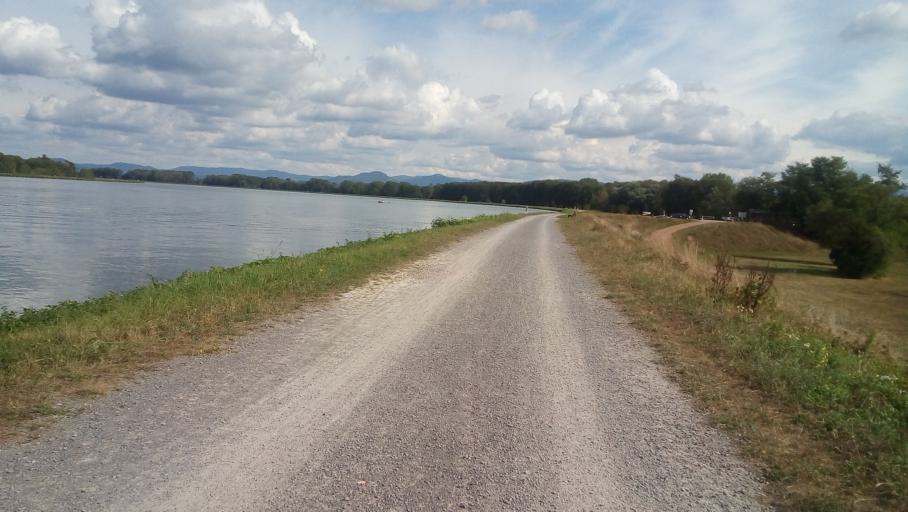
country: DE
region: Baden-Wuerttemberg
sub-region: Karlsruhe Region
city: Schwarzach
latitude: 48.7890
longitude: 8.0501
